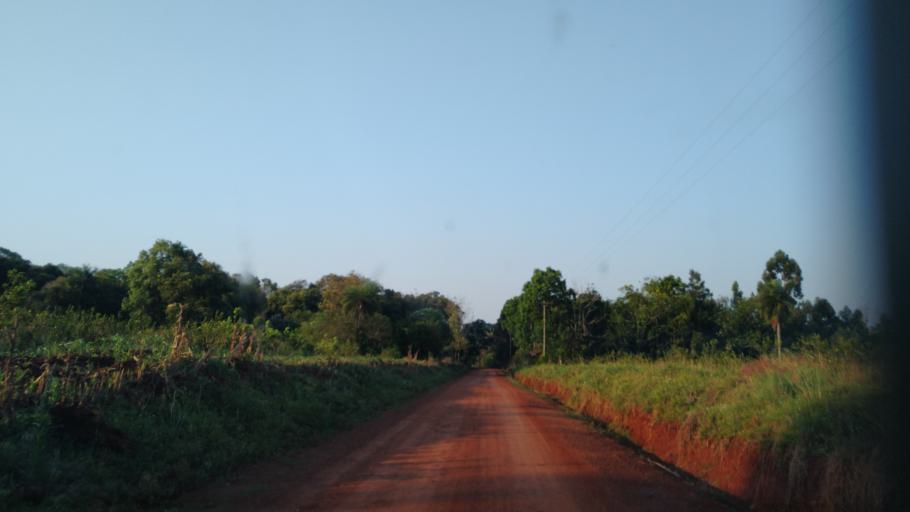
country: AR
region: Misiones
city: Jardin America
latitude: -27.0799
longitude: -55.2730
